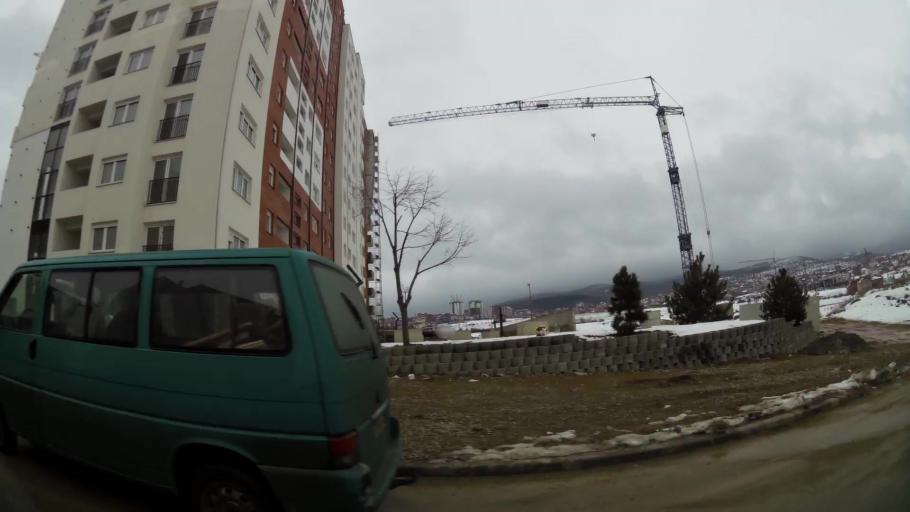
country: XK
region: Pristina
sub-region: Komuna e Prishtines
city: Pristina
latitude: 42.6483
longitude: 21.1823
